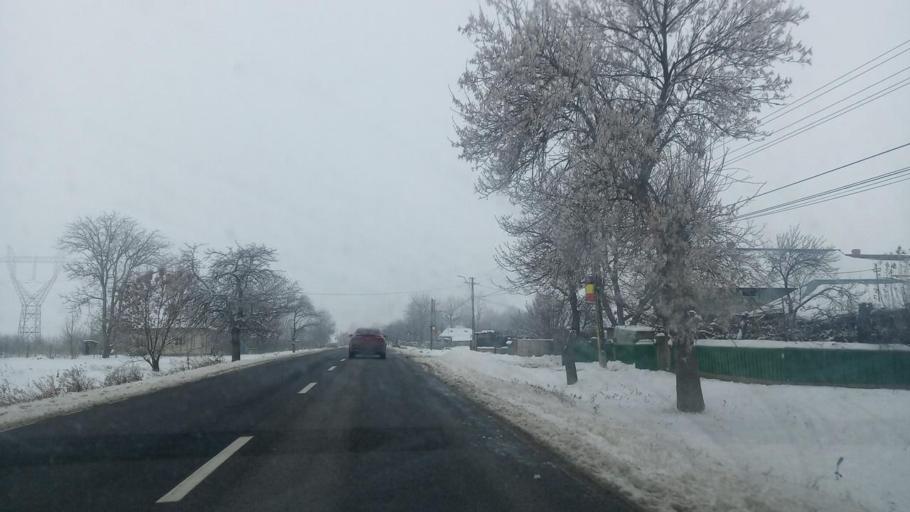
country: RO
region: Iasi
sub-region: Comuna Ciohorani
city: Ciohorani
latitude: 47.1194
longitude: 26.6760
